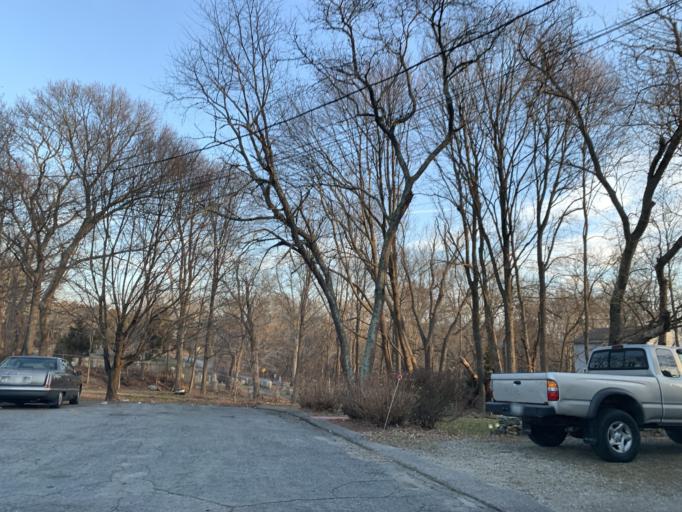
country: US
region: Rhode Island
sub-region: Washington County
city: Wakefield-Peacedale
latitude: 41.4473
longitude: -71.5013
